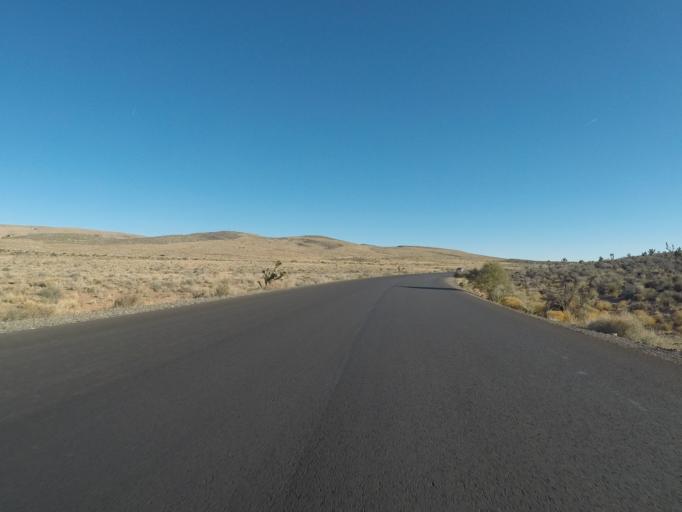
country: US
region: Nevada
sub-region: Clark County
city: Summerlin South
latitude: 36.1151
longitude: -115.4514
